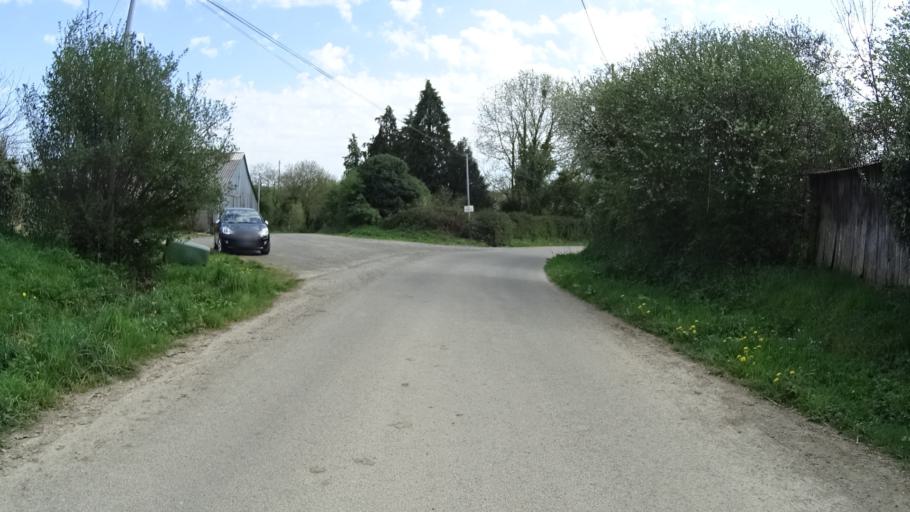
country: FR
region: Brittany
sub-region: Departement du Finistere
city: Sizun
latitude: 48.4214
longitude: -4.0552
